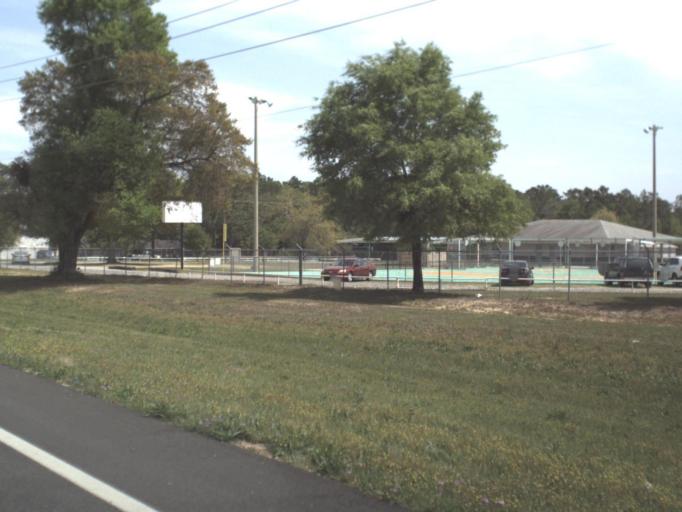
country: US
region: Florida
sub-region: Escambia County
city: Ensley
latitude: 30.5326
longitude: -87.2512
